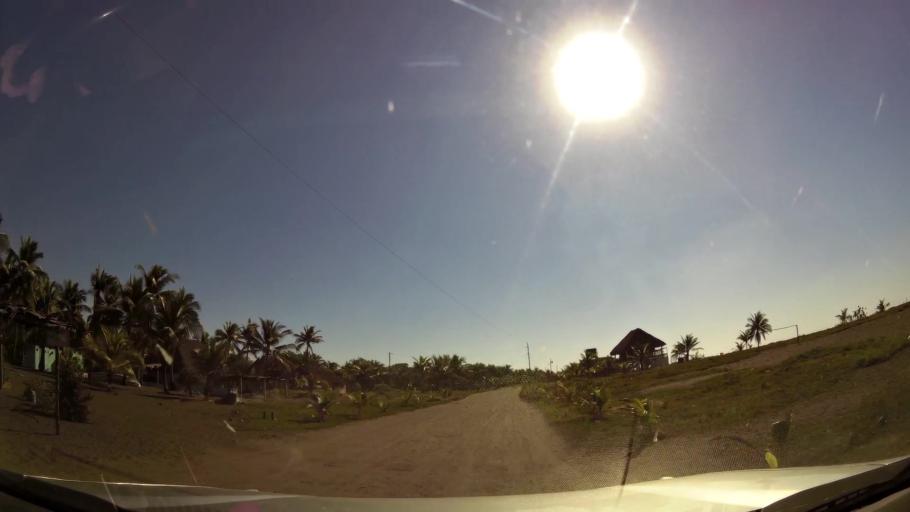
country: GT
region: Jutiapa
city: Pasaco
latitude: 13.8540
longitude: -90.3839
